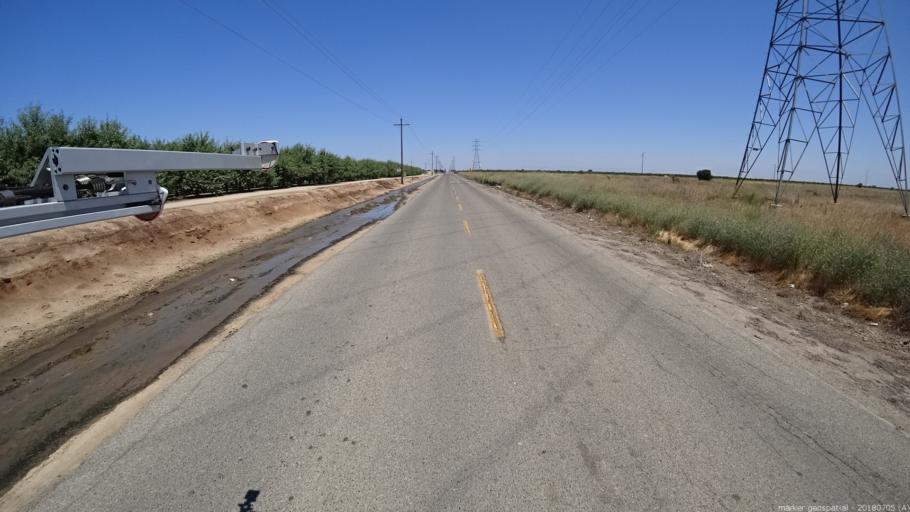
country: US
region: California
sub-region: Madera County
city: Fairmead
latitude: 37.1247
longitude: -120.2022
